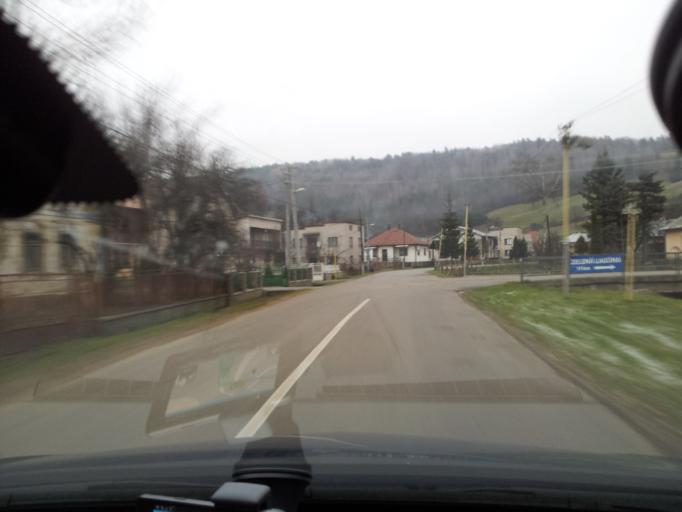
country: SK
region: Presovsky
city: Giraltovce
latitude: 49.0614
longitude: 21.5817
